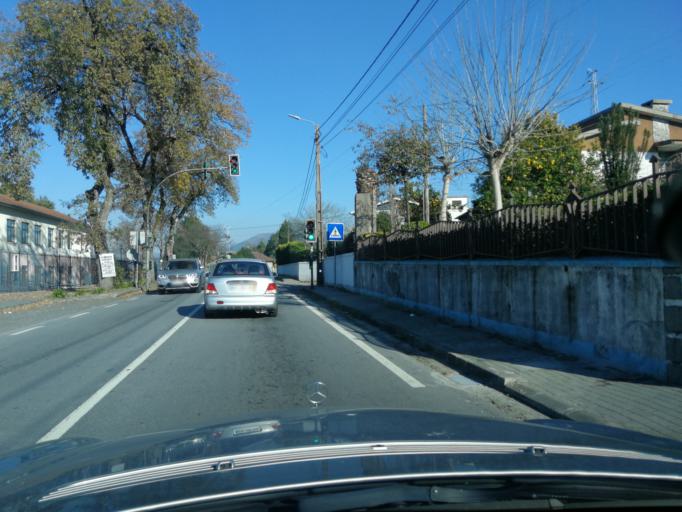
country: PT
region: Braga
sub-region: Braga
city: Adaufe
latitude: 41.6129
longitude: -8.4165
